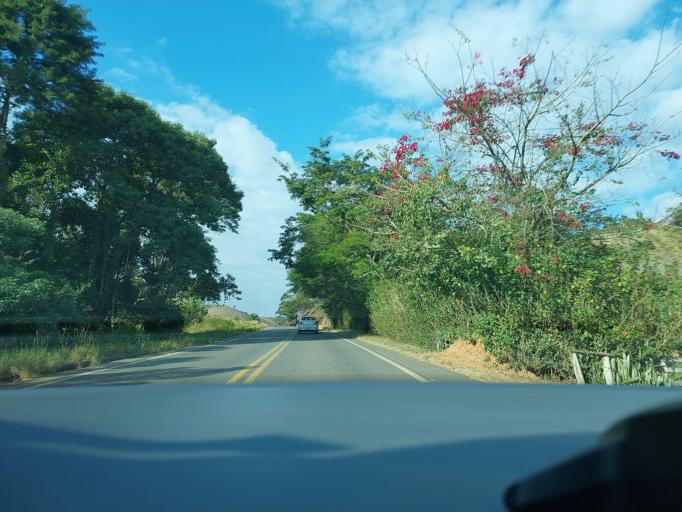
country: BR
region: Minas Gerais
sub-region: Vicosa
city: Vicosa
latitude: -20.8273
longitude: -42.7775
